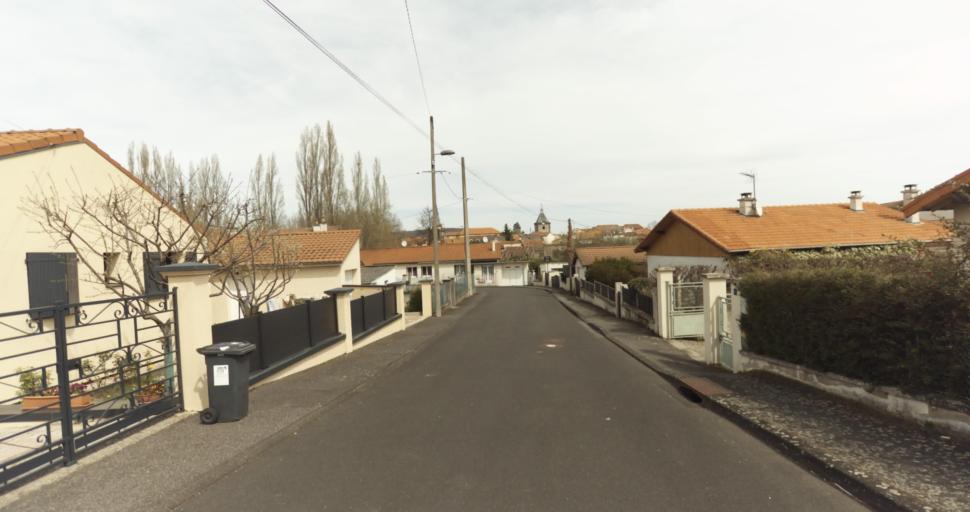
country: FR
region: Auvergne
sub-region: Departement du Puy-de-Dome
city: Cebazat
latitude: 45.8286
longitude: 3.0992
